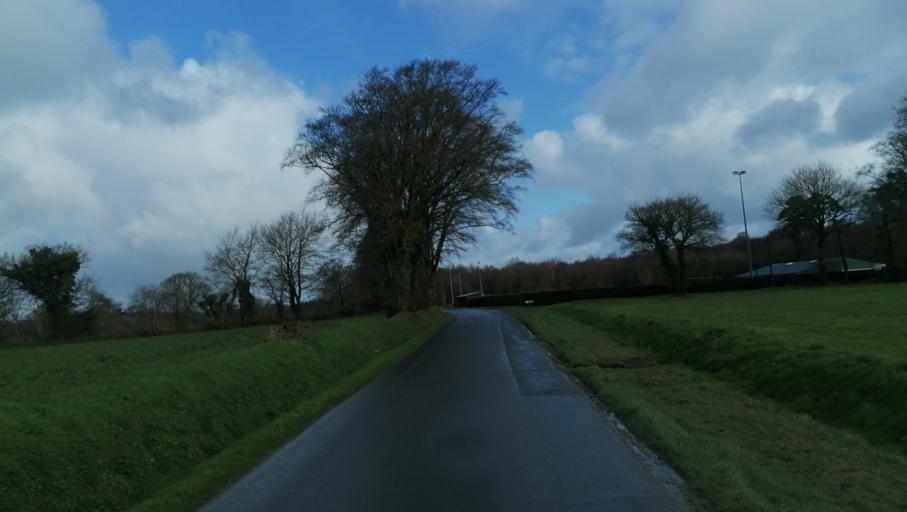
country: FR
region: Brittany
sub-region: Departement des Cotes-d'Armor
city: Lanrodec
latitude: 48.5013
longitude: -3.0296
